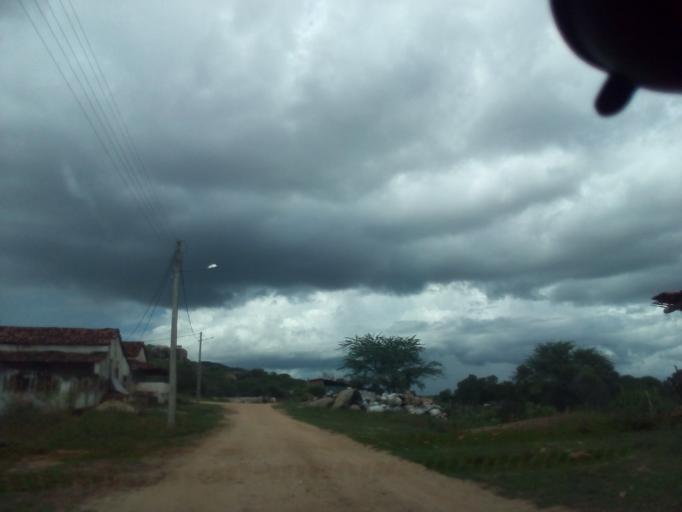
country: BR
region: Rio Grande do Norte
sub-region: Sao Tome
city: Sao Tome
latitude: -5.9504
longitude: -35.9255
